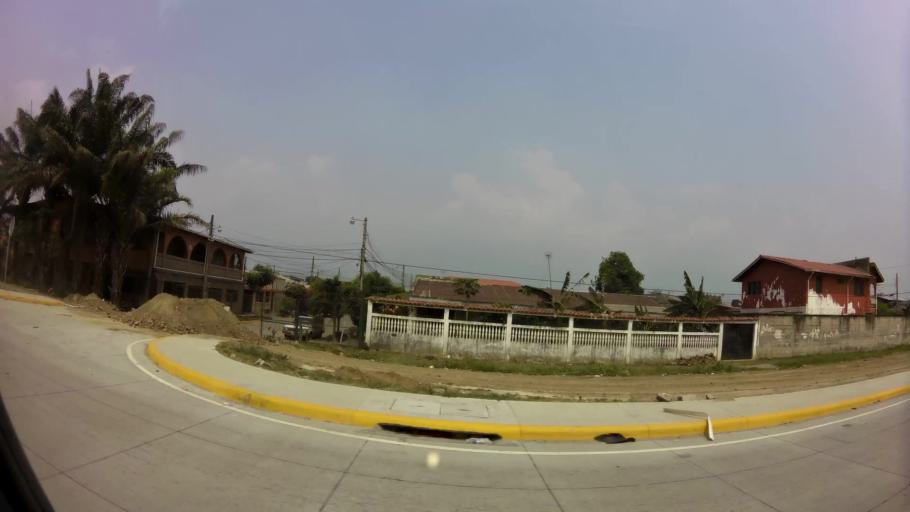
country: HN
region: Cortes
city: San Pedro Sula
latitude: 15.5089
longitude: -88.0035
